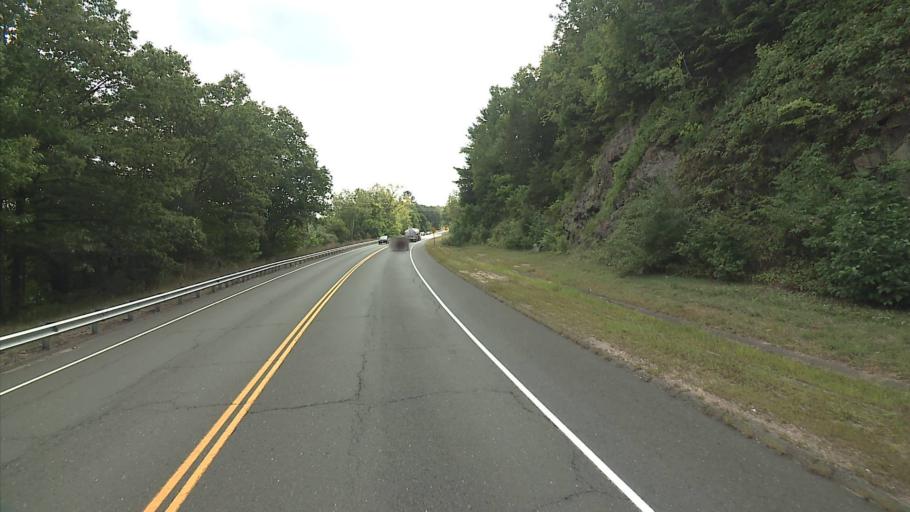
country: US
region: Connecticut
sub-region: Hartford County
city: Tariffville
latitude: 41.9013
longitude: -72.7585
